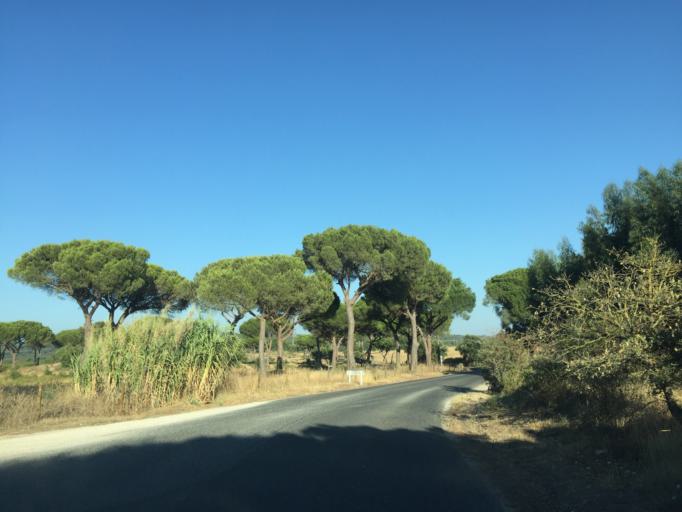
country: PT
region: Lisbon
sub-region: Azambuja
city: Aveiras de Cima
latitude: 39.1097
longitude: -8.9648
